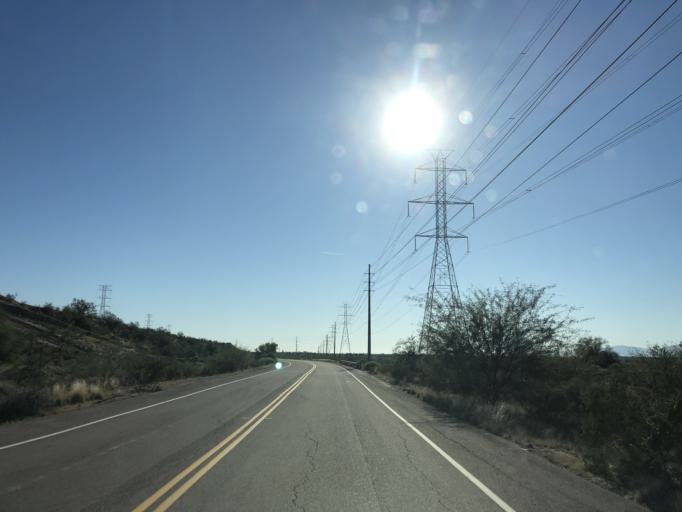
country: US
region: Arizona
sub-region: Maricopa County
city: Sun City West
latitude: 33.6939
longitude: -112.2934
